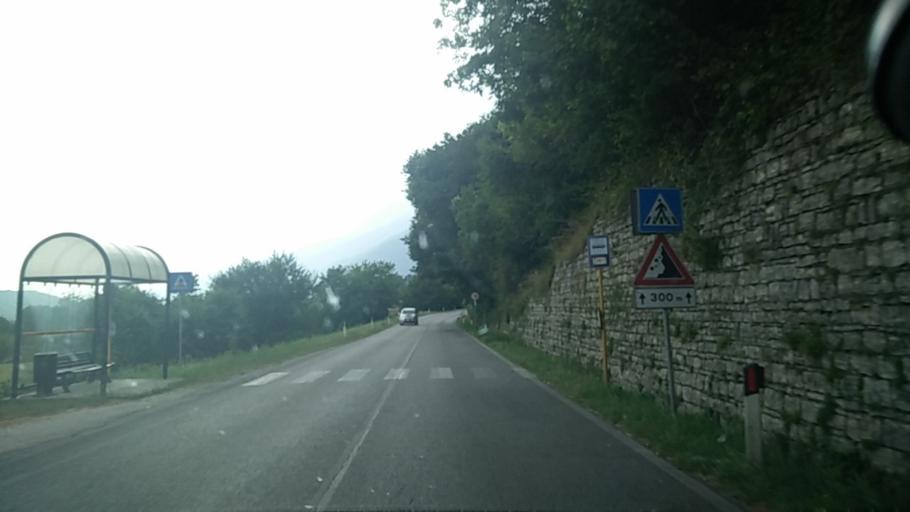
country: IT
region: Veneto
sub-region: Provincia di Treviso
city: Cison di Valmarino
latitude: 45.9721
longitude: 12.1683
